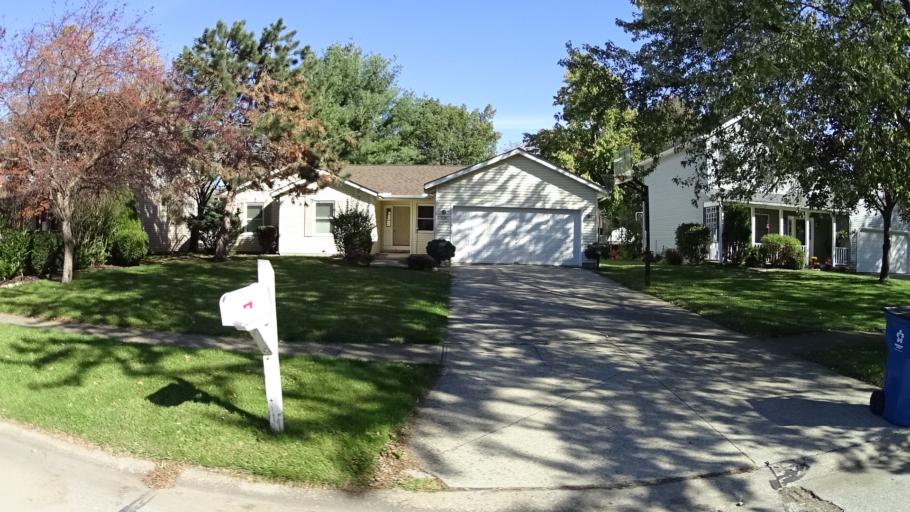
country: US
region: Ohio
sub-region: Lorain County
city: Lorain
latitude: 41.4125
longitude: -82.1746
